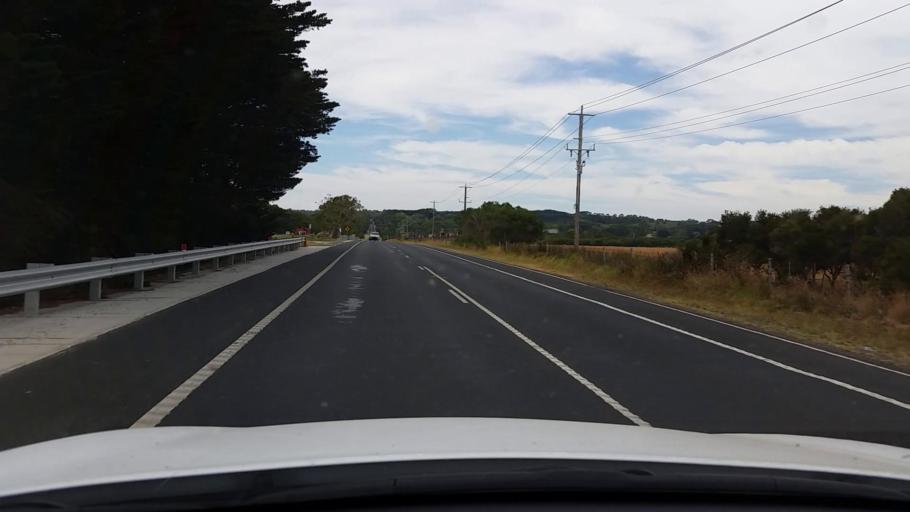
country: AU
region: Victoria
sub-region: Mornington Peninsula
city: Safety Beach
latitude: -38.3138
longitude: 145.0221
